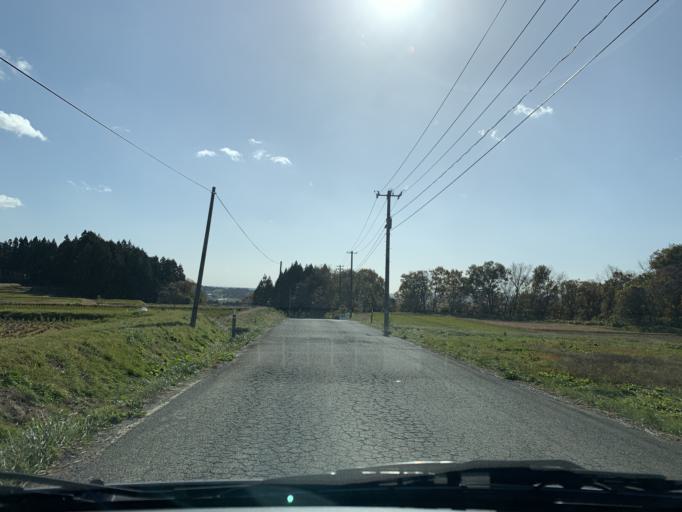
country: JP
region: Iwate
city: Ichinoseki
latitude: 39.0245
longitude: 141.1240
